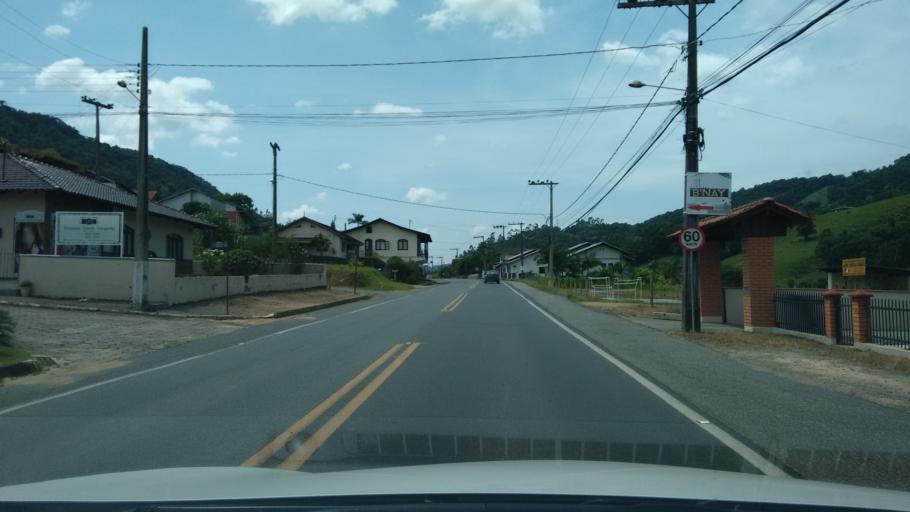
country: BR
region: Santa Catarina
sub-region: Rodeio
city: Gavea
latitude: -26.9045
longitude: -49.3604
